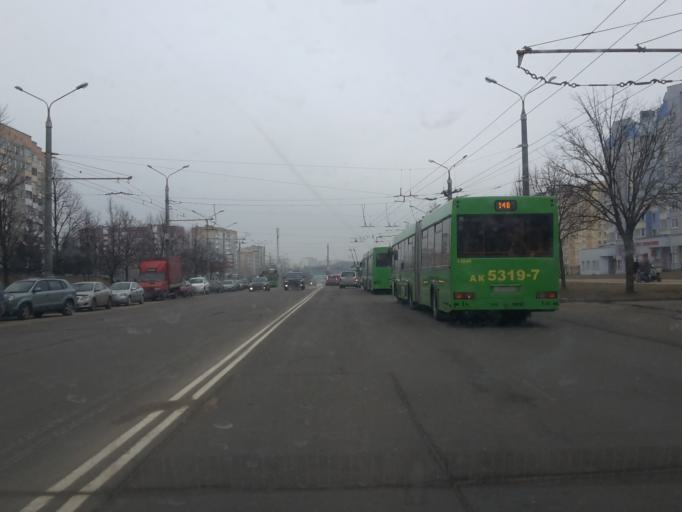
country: BY
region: Minsk
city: Novoye Medvezhino
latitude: 53.9029
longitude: 27.4354
